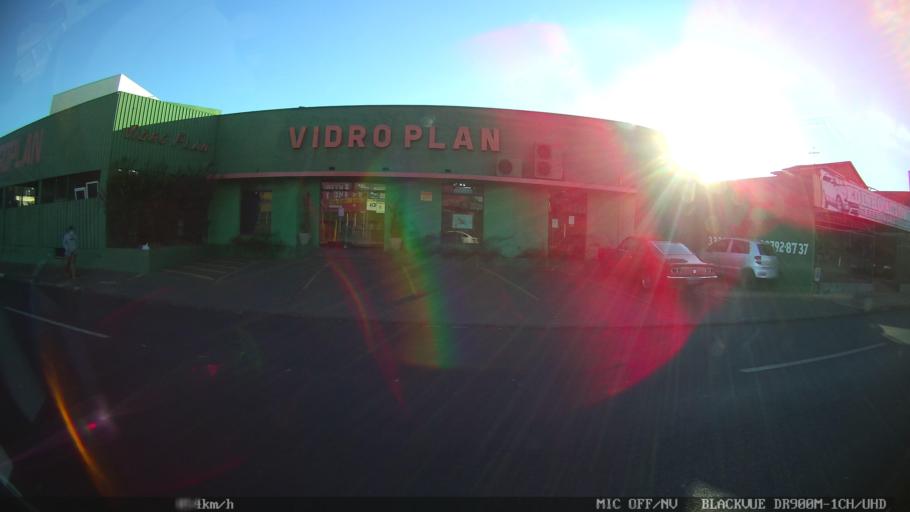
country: BR
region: Sao Paulo
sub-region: Araraquara
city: Araraquara
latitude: -21.7888
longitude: -48.1723
